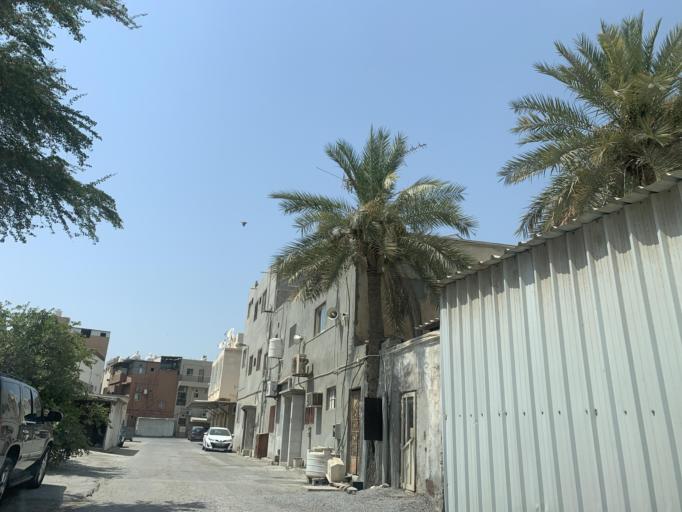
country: BH
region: Manama
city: Jidd Hafs
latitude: 26.2063
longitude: 50.5566
